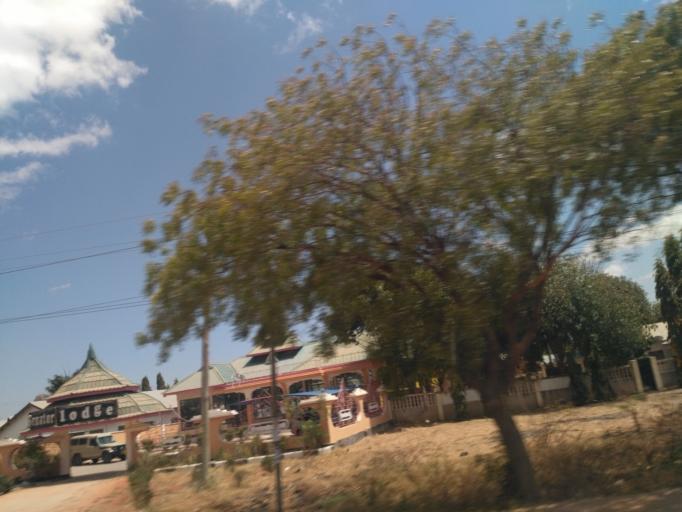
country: TZ
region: Dodoma
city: Kisasa
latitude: -6.1684
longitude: 35.7786
